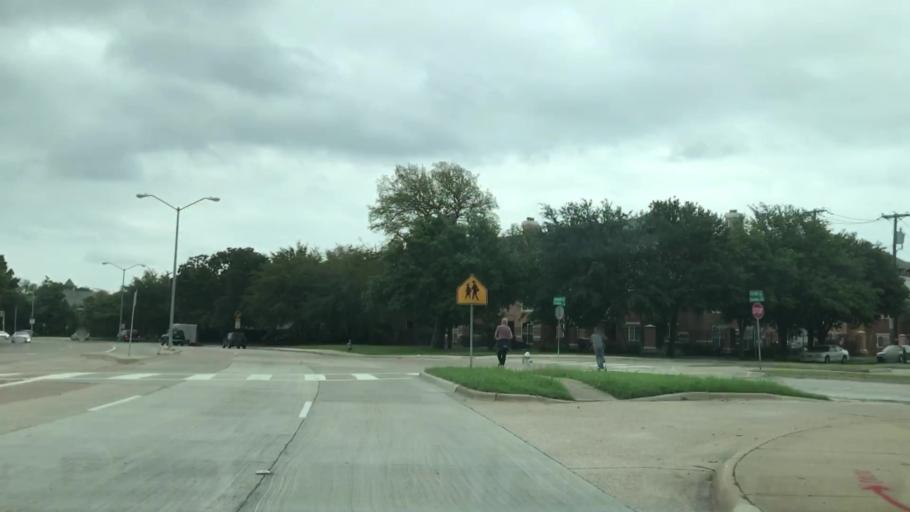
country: US
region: Texas
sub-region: Dallas County
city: Dallas
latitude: 32.8024
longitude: -96.7901
